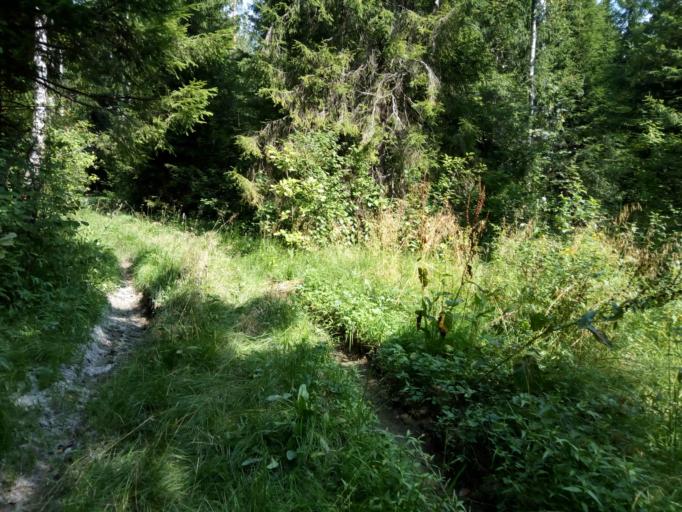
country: RU
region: Moskovskaya
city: Kubinka
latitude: 55.5932
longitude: 36.7289
